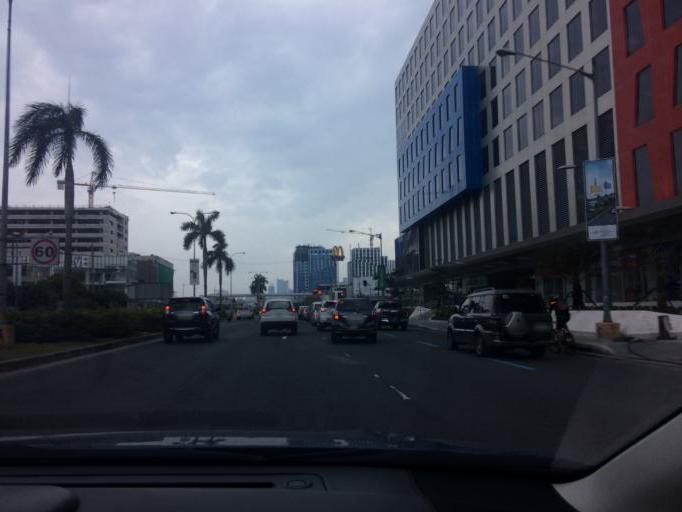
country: PH
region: Metro Manila
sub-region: Makati City
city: Makati City
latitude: 14.5351
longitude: 120.9892
